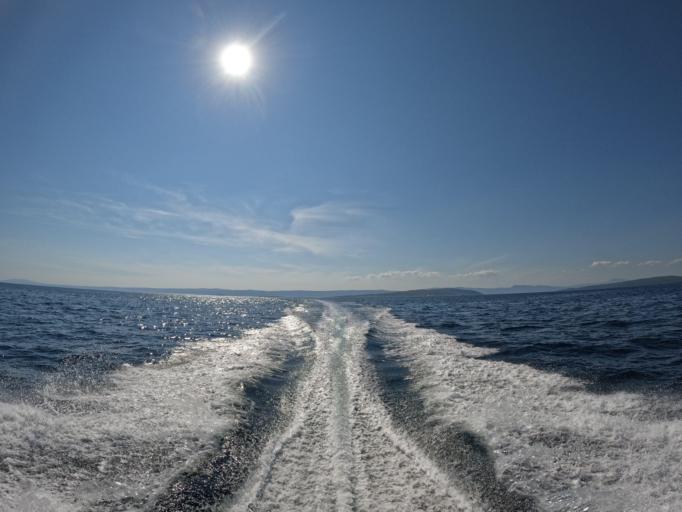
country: HR
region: Primorsko-Goranska
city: Punat
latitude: 44.9568
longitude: 14.6130
